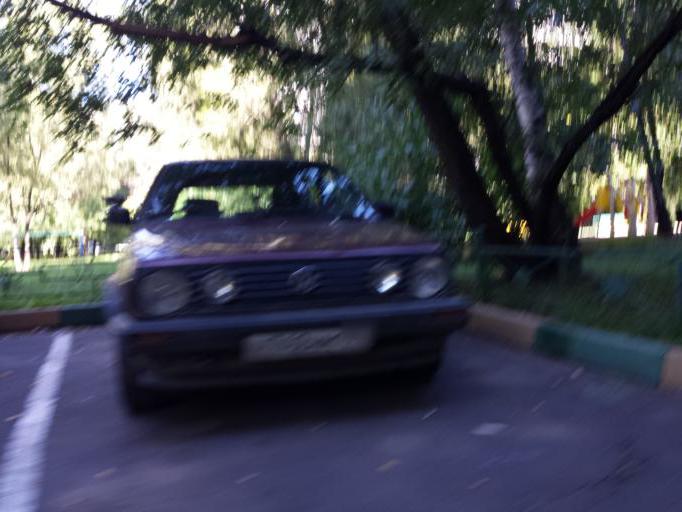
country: RU
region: Moskovskaya
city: Novogireyevo
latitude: 55.7468
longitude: 37.8248
